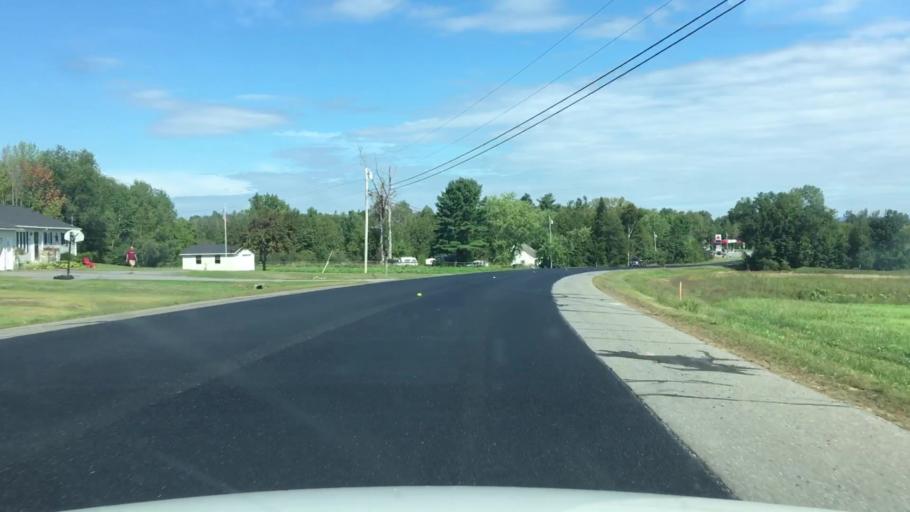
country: US
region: Maine
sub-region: Penobscot County
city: Corinna
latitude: 44.9093
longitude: -69.2652
